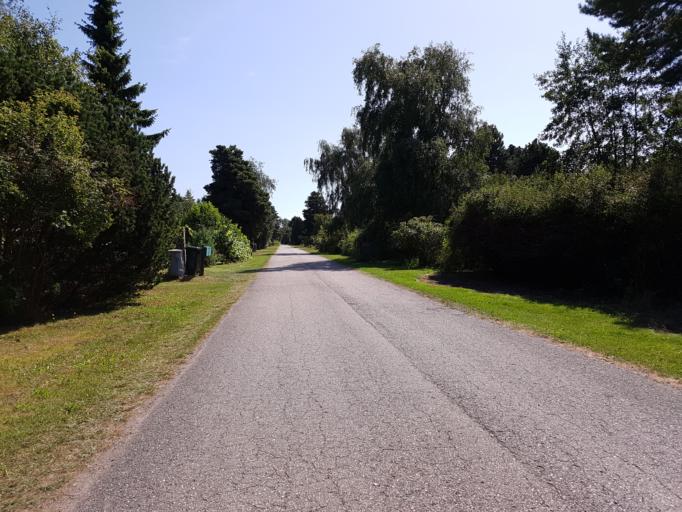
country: DK
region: Zealand
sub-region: Guldborgsund Kommune
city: Nykobing Falster
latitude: 54.5960
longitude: 11.9605
